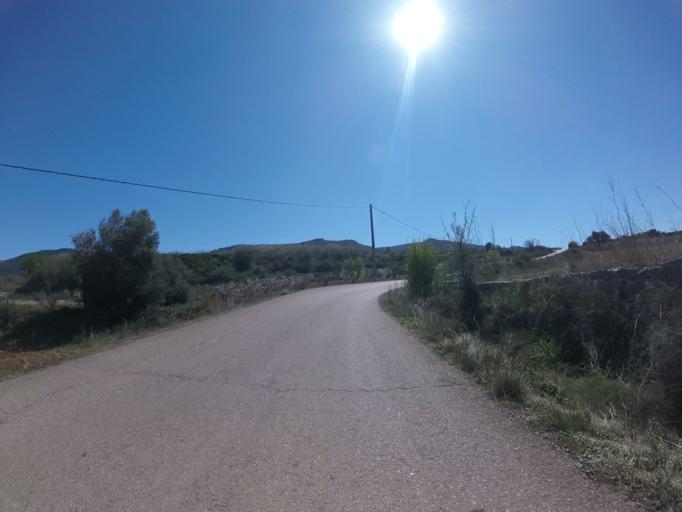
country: ES
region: Valencia
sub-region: Provincia de Castello
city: Chert/Xert
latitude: 40.4116
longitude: 0.1745
